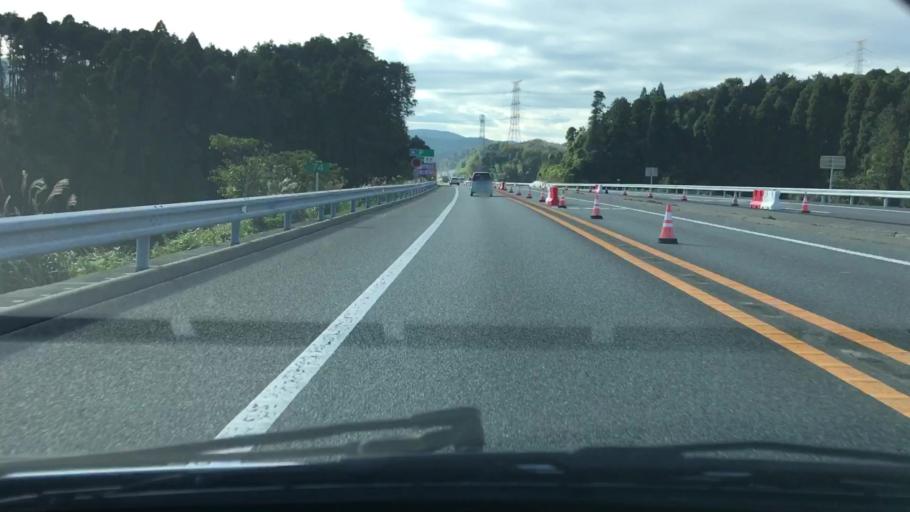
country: JP
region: Chiba
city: Kimitsu
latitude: 35.2899
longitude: 139.9297
